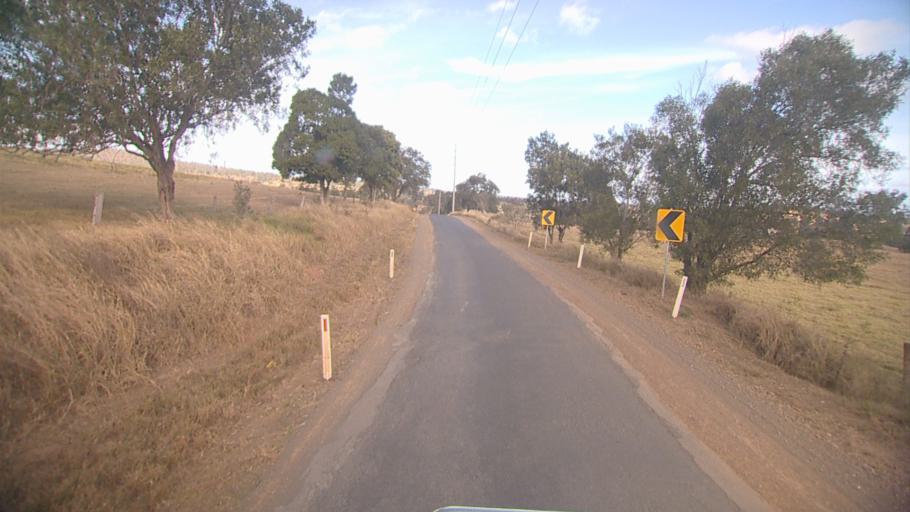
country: AU
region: Queensland
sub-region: Logan
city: Cedar Vale
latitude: -27.9098
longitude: 153.0134
